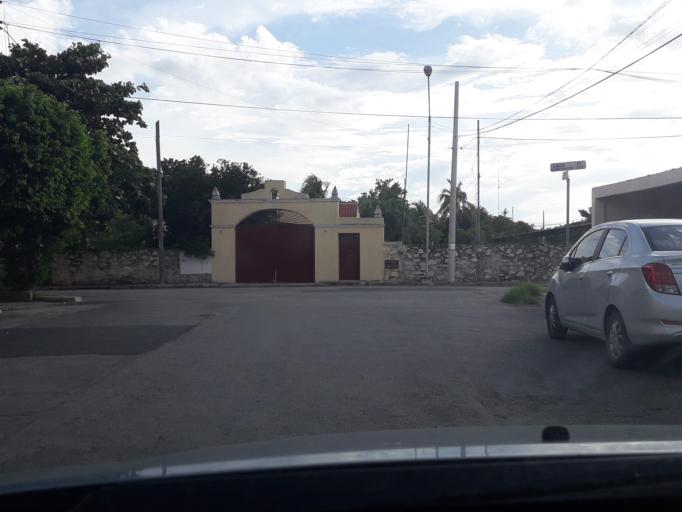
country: MX
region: Yucatan
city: Merida
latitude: 21.0068
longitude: -89.6395
